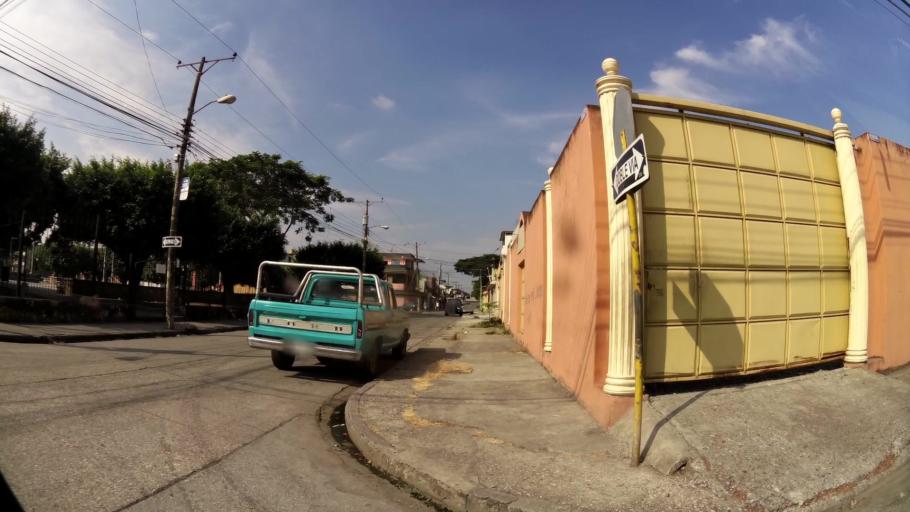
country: EC
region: Guayas
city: Guayaquil
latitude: -2.1857
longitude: -79.9115
